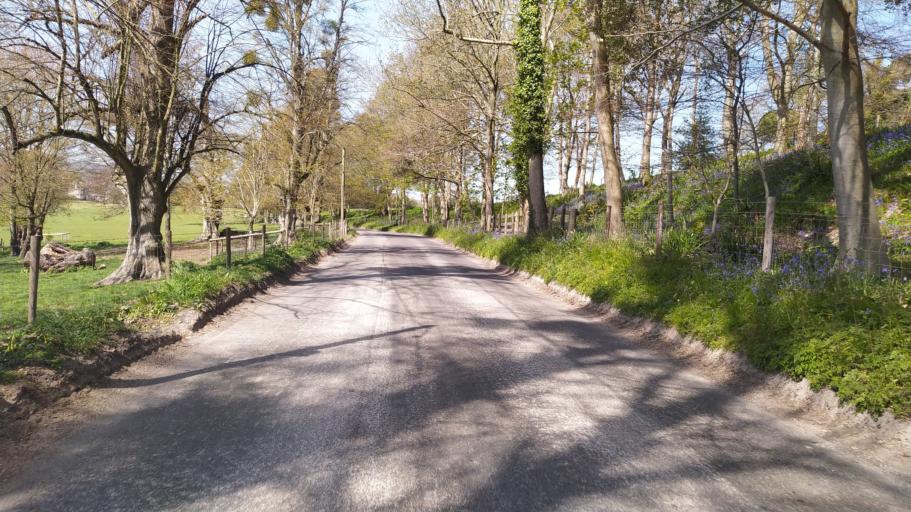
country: GB
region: England
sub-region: Dorset
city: Blandford Forum
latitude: 50.9007
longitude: -2.2126
